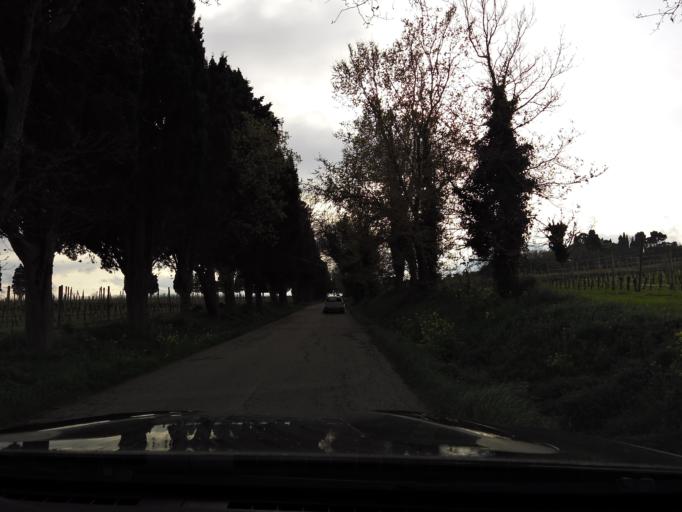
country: IT
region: The Marches
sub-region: Provincia di Macerata
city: Porto Potenza Picena
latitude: 43.3568
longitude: 13.6897
